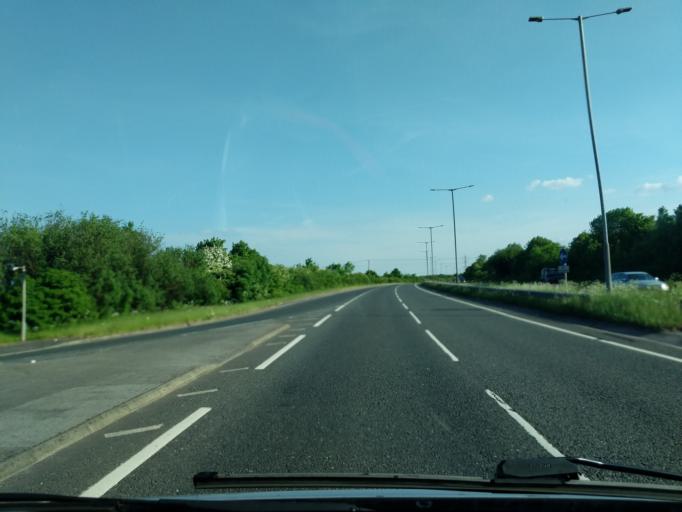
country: GB
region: England
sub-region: St. Helens
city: St Helens
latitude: 53.4116
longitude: -2.7441
